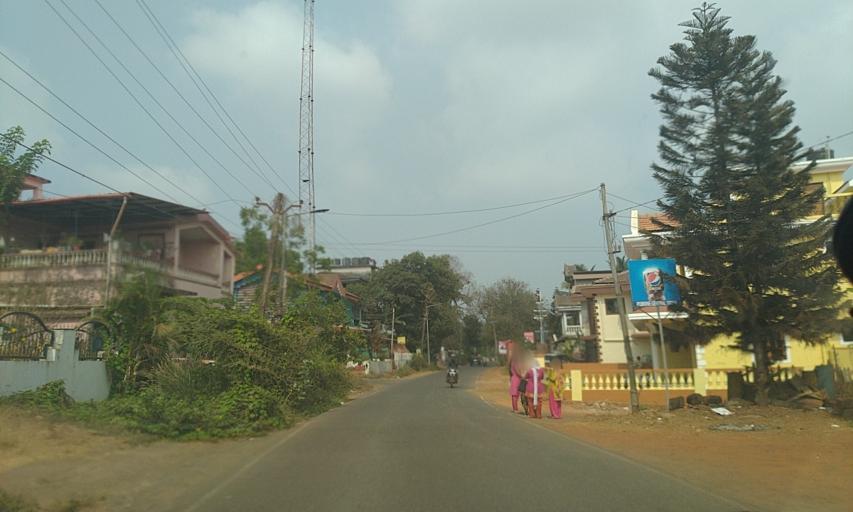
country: IN
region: Goa
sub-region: South Goa
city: Raia
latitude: 15.3070
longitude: 73.9512
